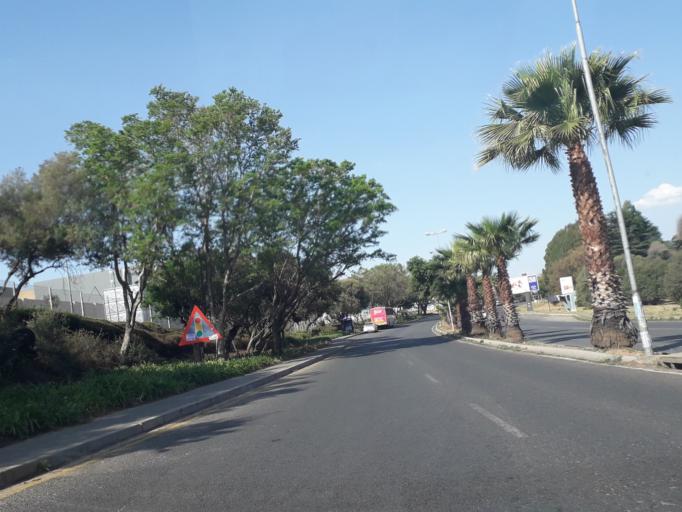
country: ZA
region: Gauteng
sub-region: West Rand District Municipality
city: Muldersdriseloop
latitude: -26.0635
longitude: 27.9467
